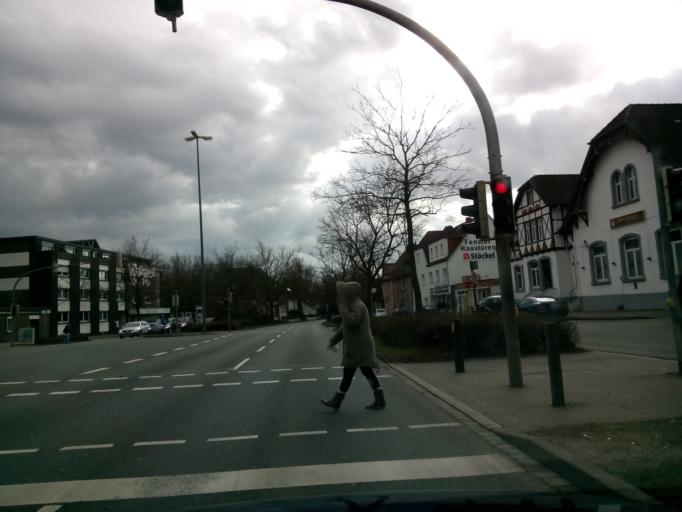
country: DE
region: Lower Saxony
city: Osnabrueck
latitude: 52.2998
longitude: 8.0354
